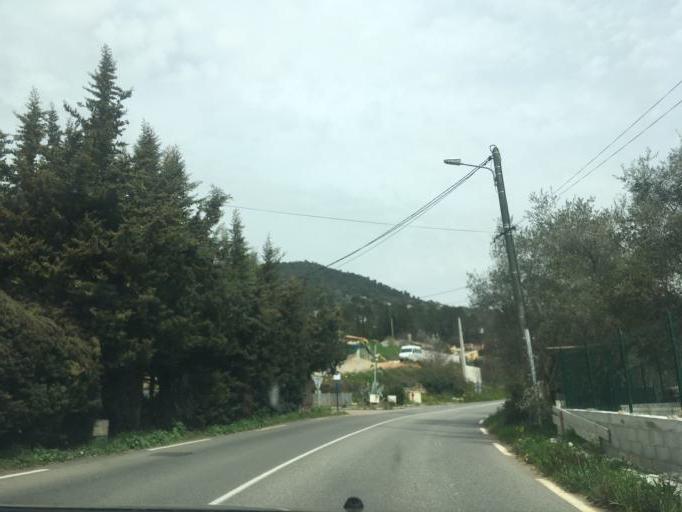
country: FR
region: Provence-Alpes-Cote d'Azur
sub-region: Departement des Alpes-Maritimes
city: Le Tignet
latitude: 43.6303
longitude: 6.8384
